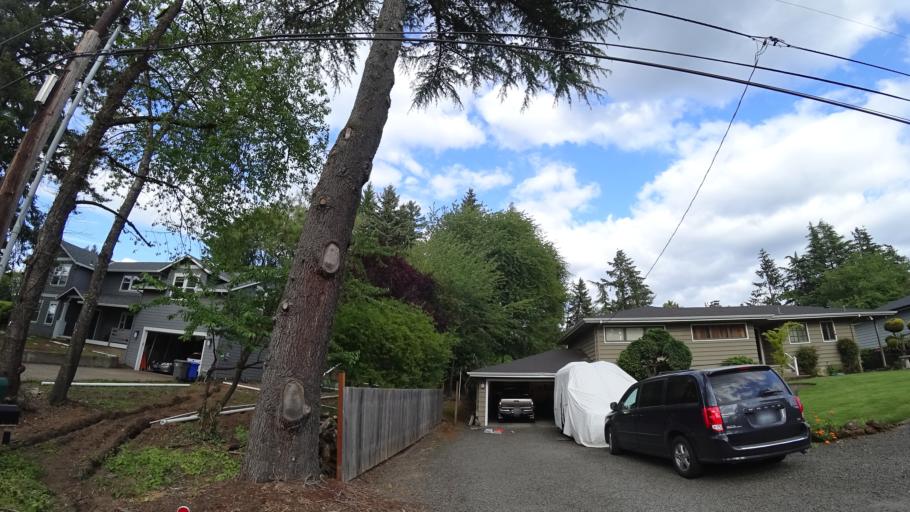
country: US
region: Oregon
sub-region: Washington County
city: Garden Home-Whitford
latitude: 45.4691
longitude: -122.7268
